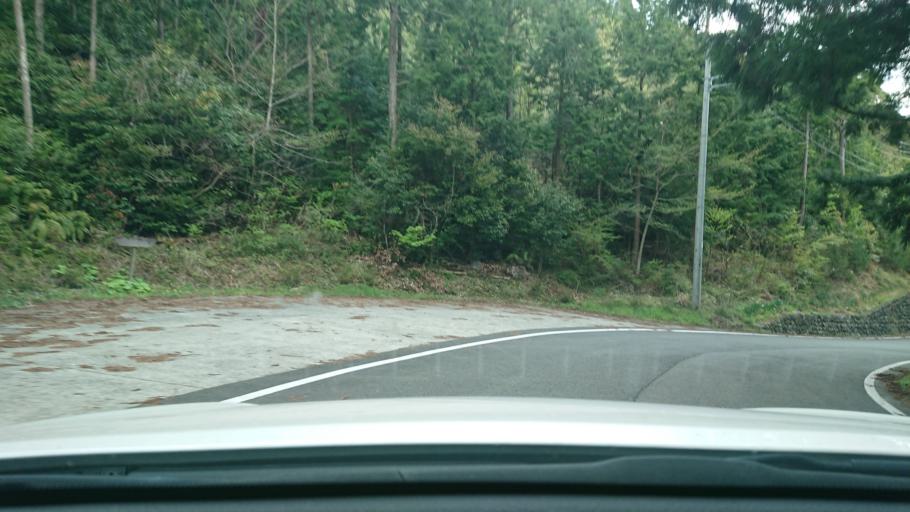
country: JP
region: Tokushima
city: Kamojimacho-jogejima
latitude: 33.8826
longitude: 134.3829
